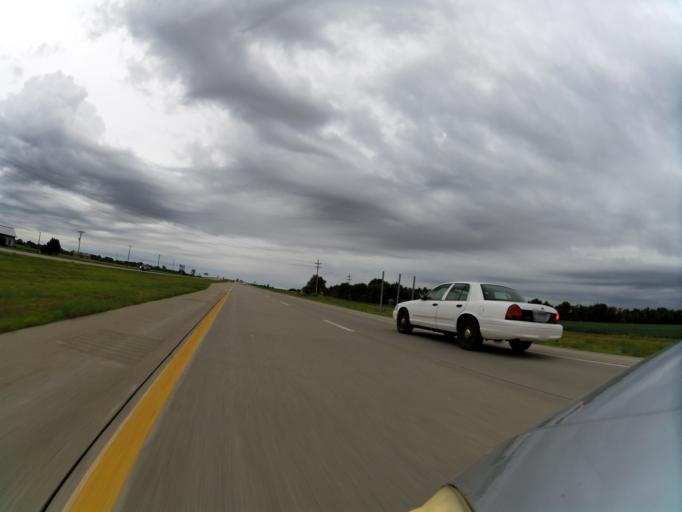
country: US
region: Kansas
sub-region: Reno County
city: South Hutchinson
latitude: 37.9461
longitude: -97.8859
